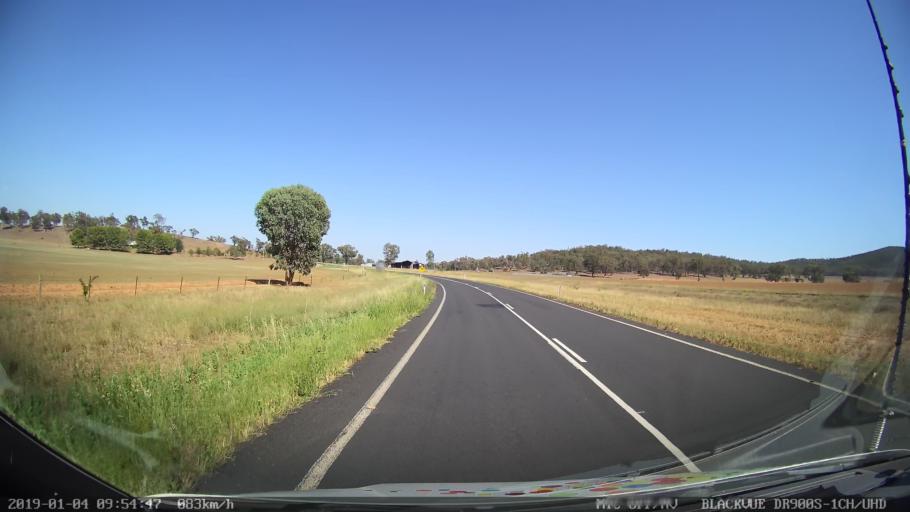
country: AU
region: New South Wales
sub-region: Cabonne
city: Canowindra
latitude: -33.5384
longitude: 148.4110
